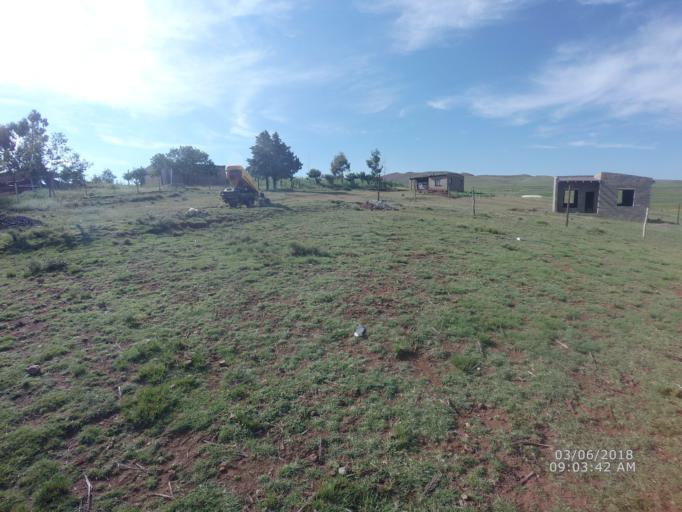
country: LS
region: Berea
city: Teyateyaneng
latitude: -29.2238
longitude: 27.8589
